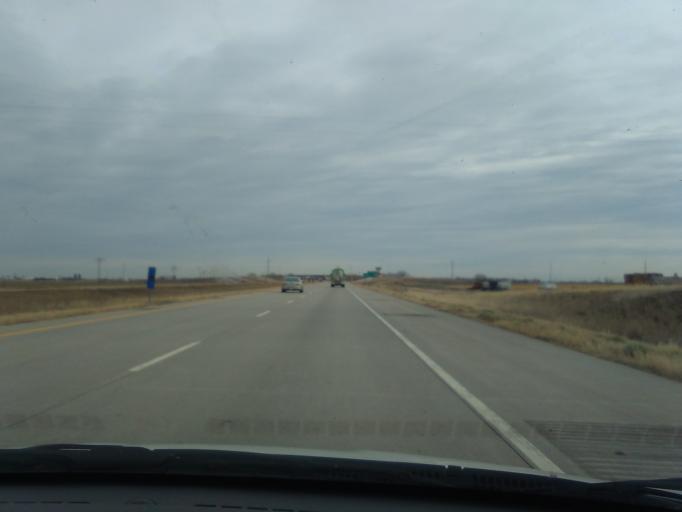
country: US
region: Colorado
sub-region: Morgan County
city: Fort Morgan
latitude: 40.2322
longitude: -104.1016
